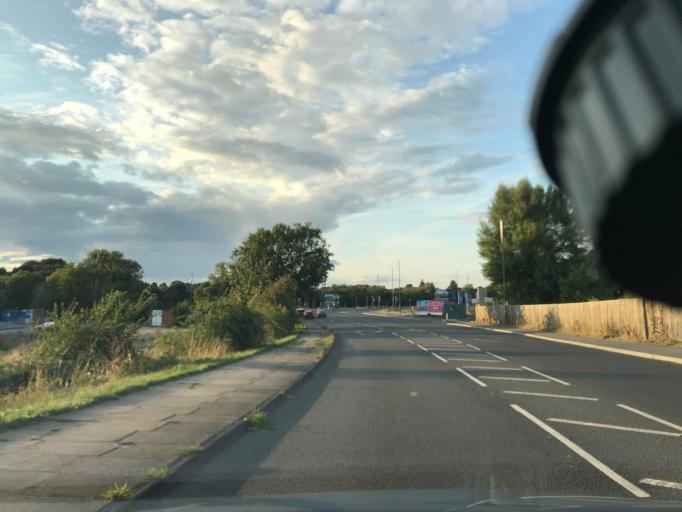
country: GB
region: England
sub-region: Buckinghamshire
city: Aylesbury
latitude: 51.8197
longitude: -0.7900
